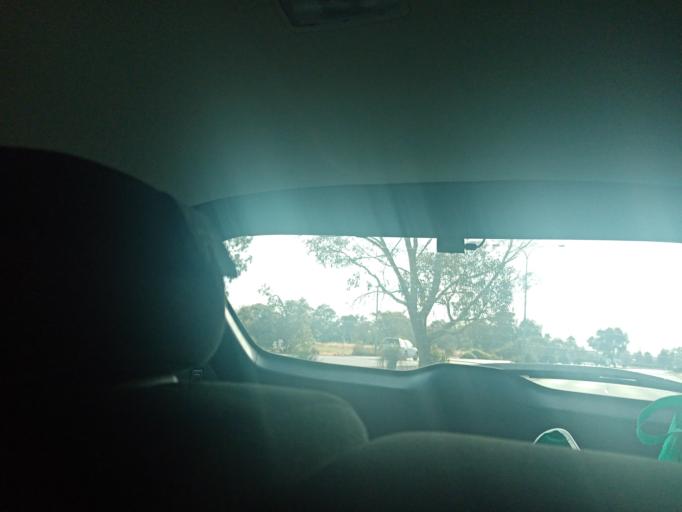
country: AU
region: Western Australia
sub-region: City of Cockburn
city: South Lake
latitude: -32.1251
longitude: 115.8366
